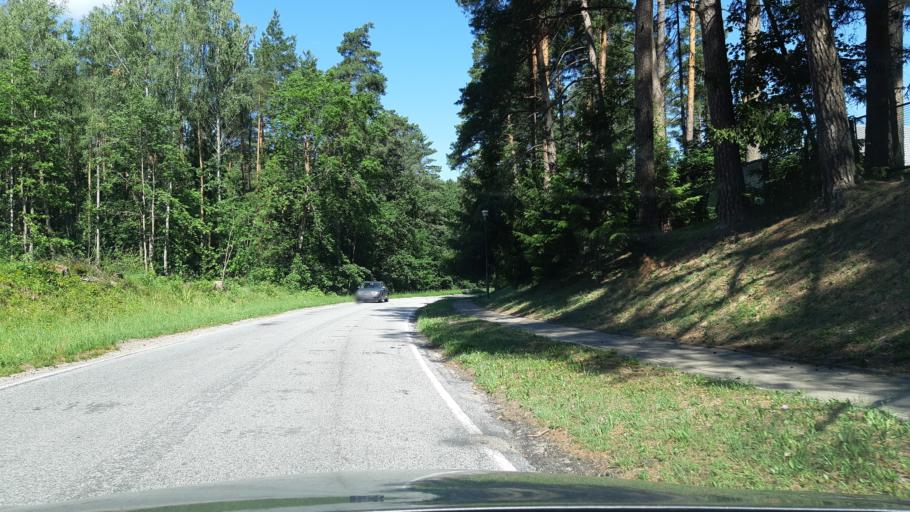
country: PL
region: Warmian-Masurian Voivodeship
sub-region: Powiat gizycki
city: Gizycko
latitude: 54.0048
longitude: 21.7382
